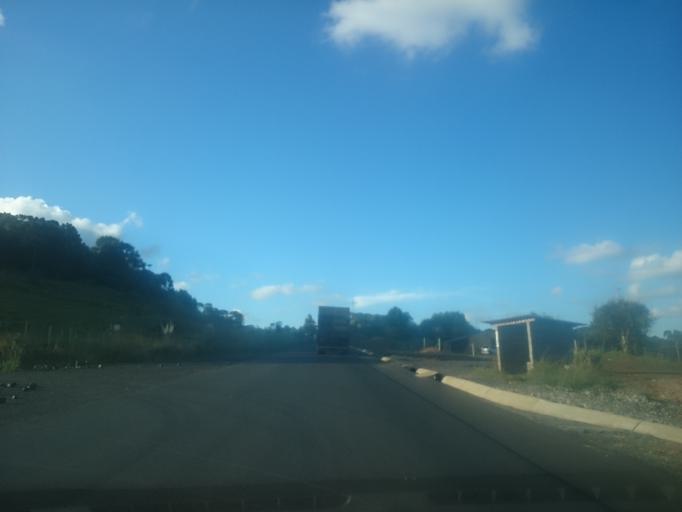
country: BR
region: Santa Catarina
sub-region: Sao Joaquim
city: Sao Joaquim
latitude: -28.0668
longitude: -50.0733
